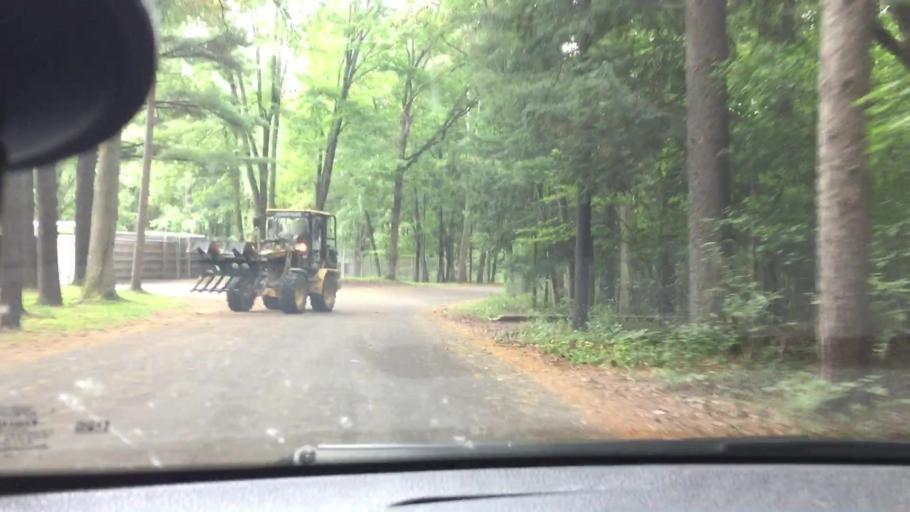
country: US
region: Wisconsin
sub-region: Chippewa County
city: Chippewa Falls
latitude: 44.9543
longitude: -91.4026
